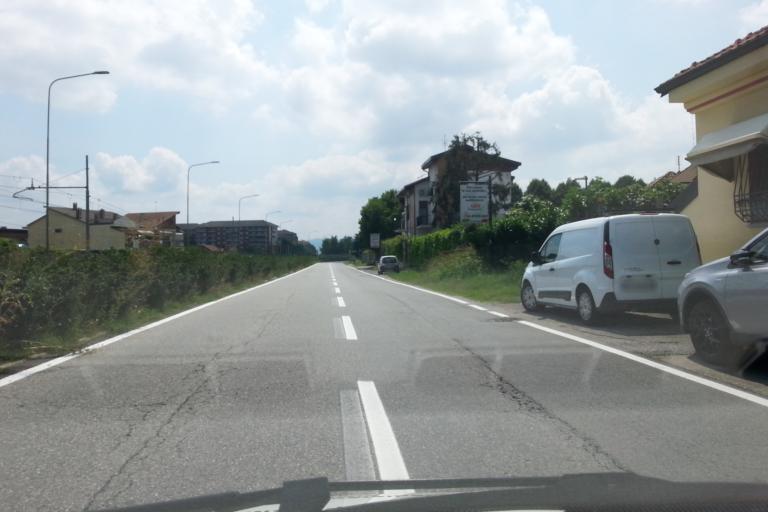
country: IT
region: Piedmont
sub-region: Provincia di Torino
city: Venaria Reale
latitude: 45.1236
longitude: 7.6412
